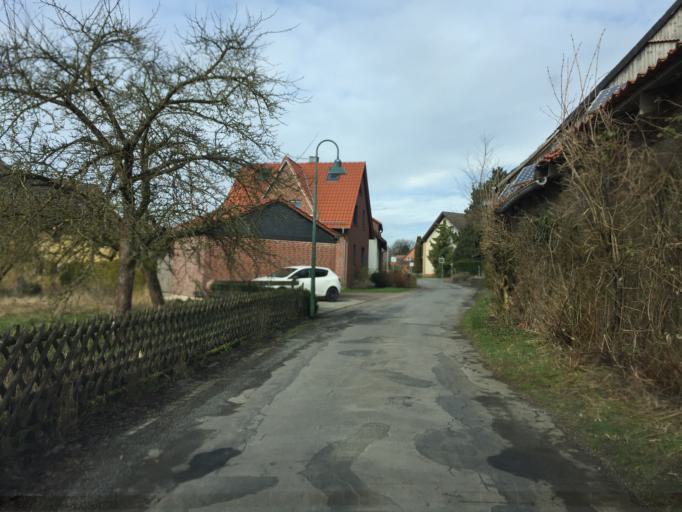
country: DE
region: Lower Saxony
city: Rinteln
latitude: 52.1038
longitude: 9.1548
